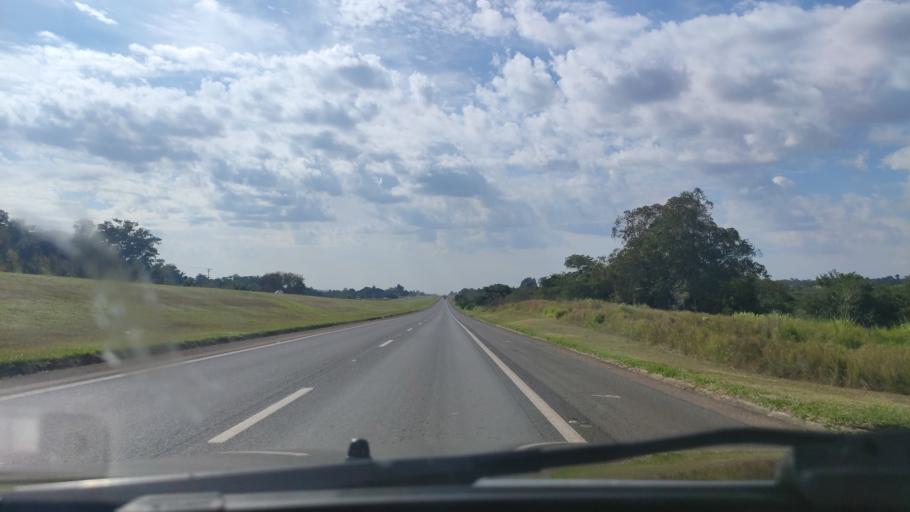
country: BR
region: Sao Paulo
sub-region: Porangaba
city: Porangaba
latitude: -23.2473
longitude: -48.0312
